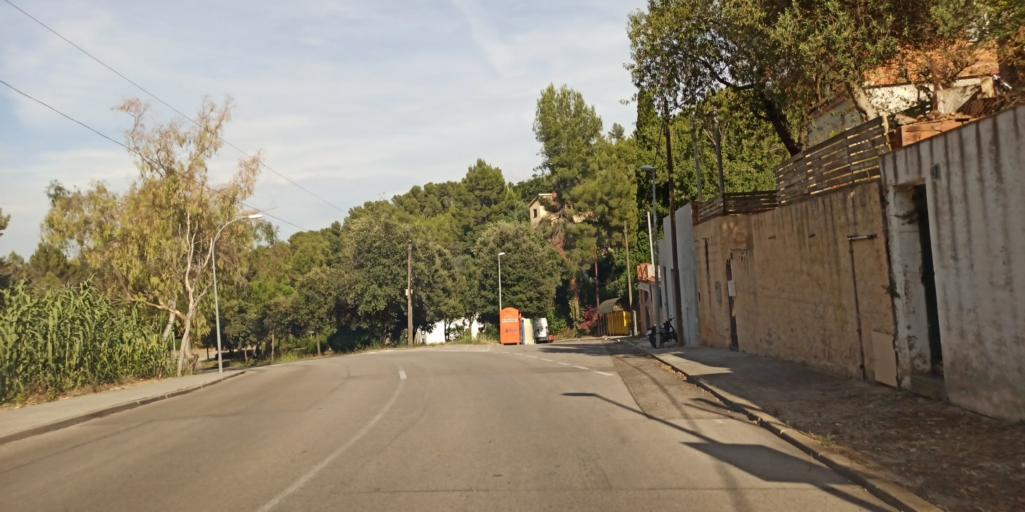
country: ES
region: Catalonia
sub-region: Provincia de Barcelona
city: Santa Coloma de Cervello
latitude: 41.3614
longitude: 2.0071
